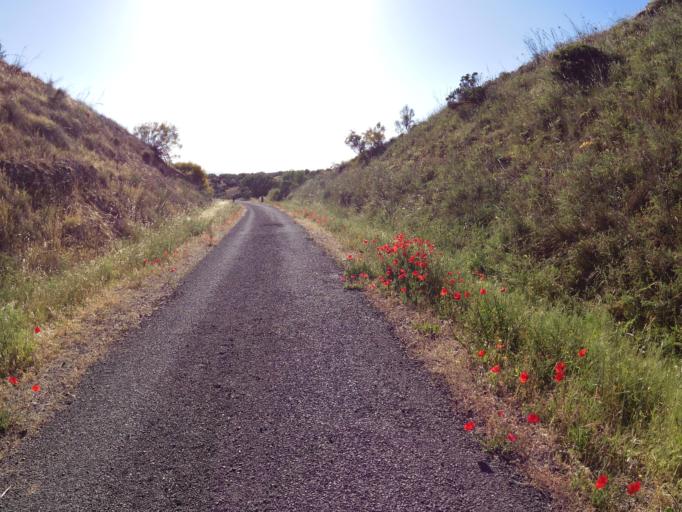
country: ES
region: Andalusia
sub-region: Province of Cordoba
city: Luque
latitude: 37.5645
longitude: -4.2428
